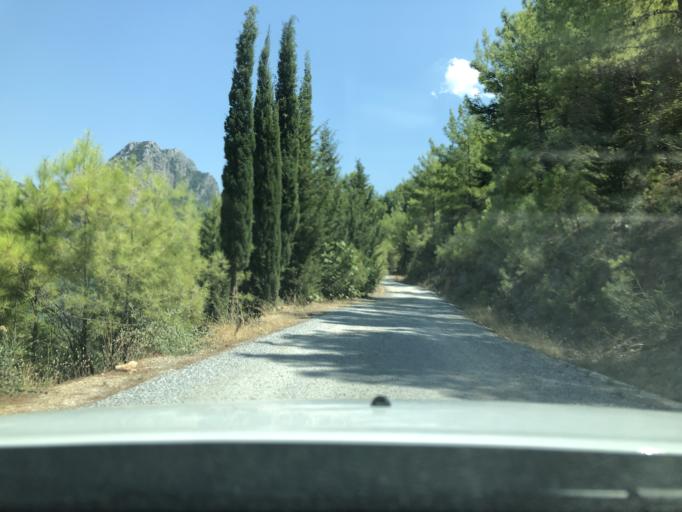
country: TR
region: Antalya
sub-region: Manavgat
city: Manavgat
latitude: 36.9060
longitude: 31.5583
